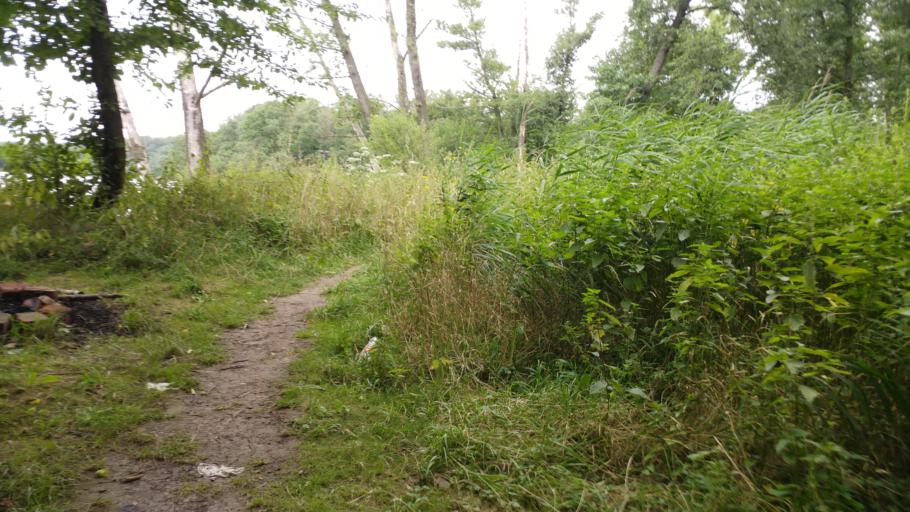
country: CZ
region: Central Bohemia
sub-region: Okres Praha-Zapad
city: Pruhonice
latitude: 50.0351
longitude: 14.5481
